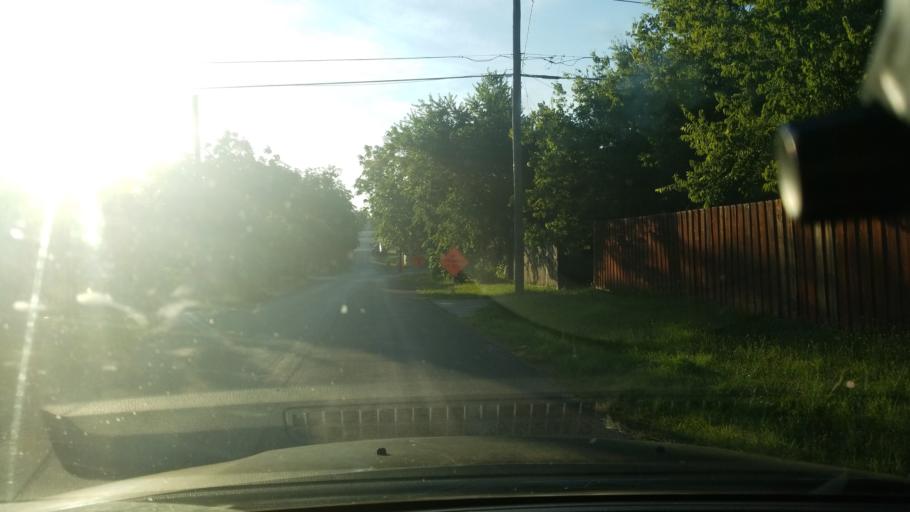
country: US
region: Texas
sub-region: Dallas County
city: Dallas
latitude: 32.7150
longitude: -96.8191
